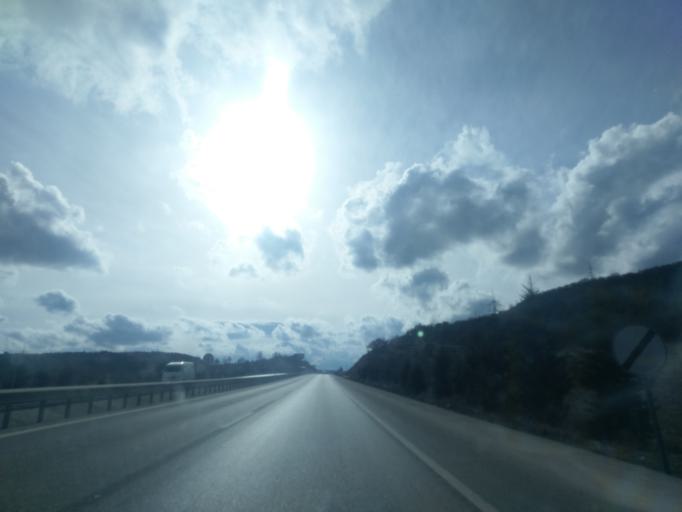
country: TR
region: Kuetahya
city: Sabuncu
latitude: 39.5890
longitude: 30.1366
